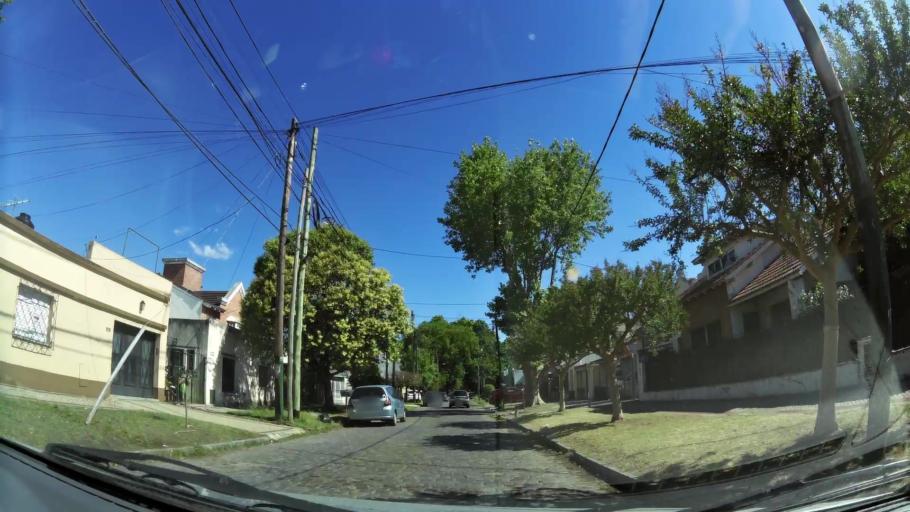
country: AR
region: Buenos Aires
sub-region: Partido de Lomas de Zamora
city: Lomas de Zamora
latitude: -34.7555
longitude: -58.4119
